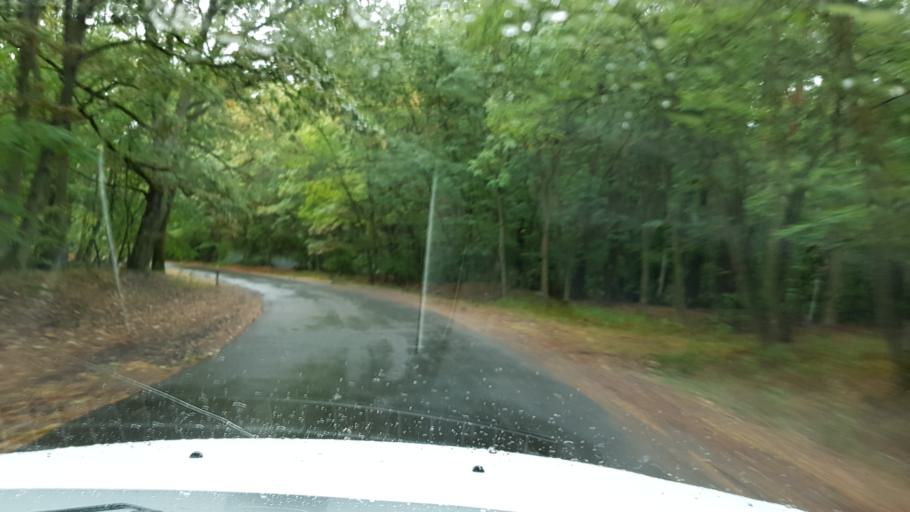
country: DE
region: Brandenburg
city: Meyenburg
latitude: 52.9754
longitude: 14.2310
